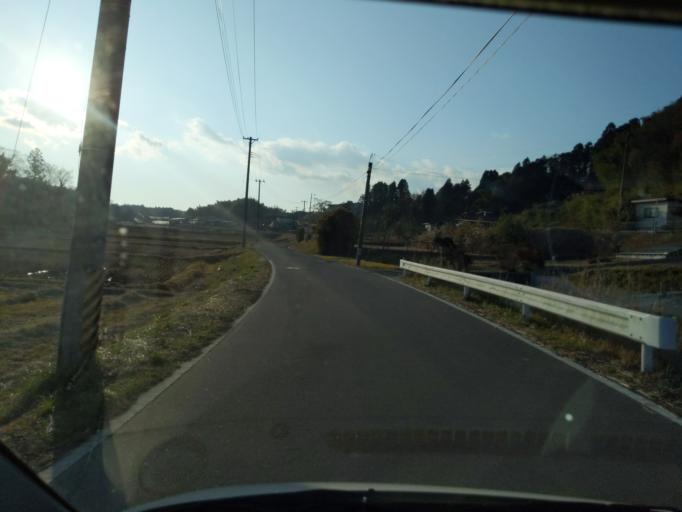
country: JP
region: Miyagi
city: Wakuya
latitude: 38.6999
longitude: 141.1143
